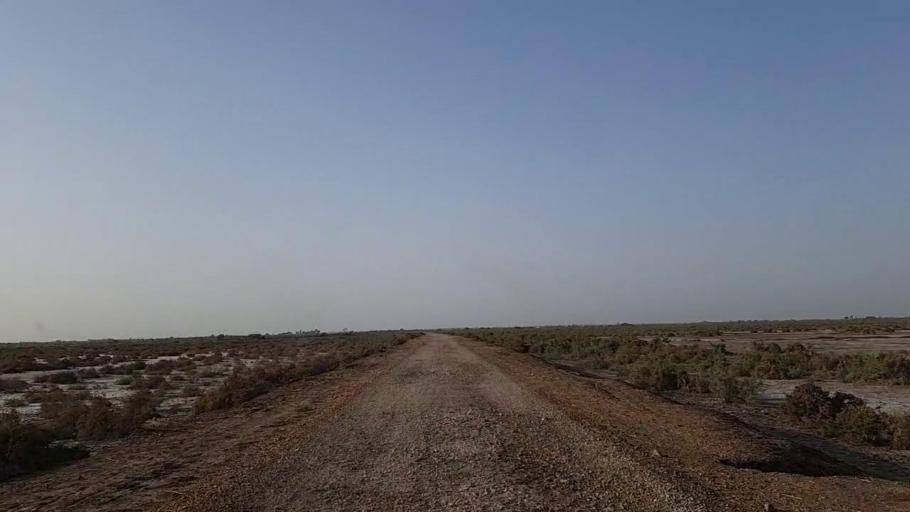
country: PK
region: Sindh
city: Jati
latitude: 24.3576
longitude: 68.1474
